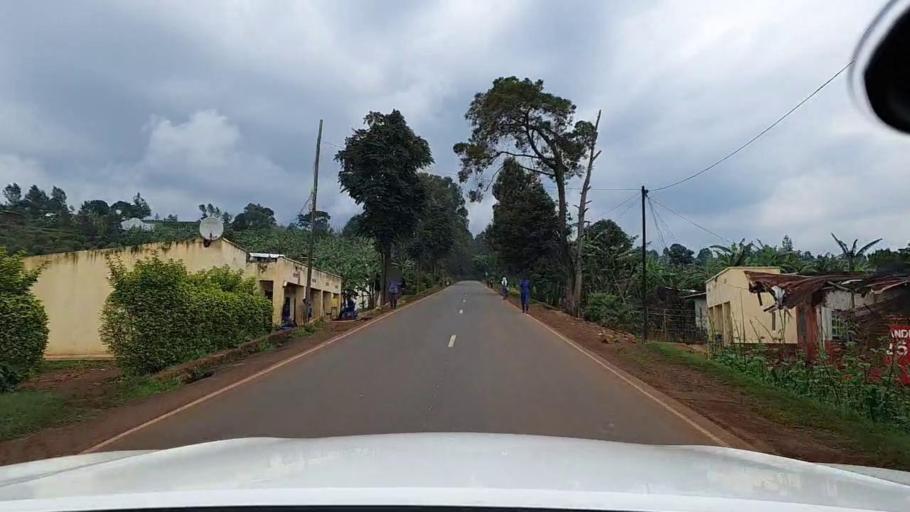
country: RW
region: Western Province
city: Cyangugu
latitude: -2.5379
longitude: 28.8963
